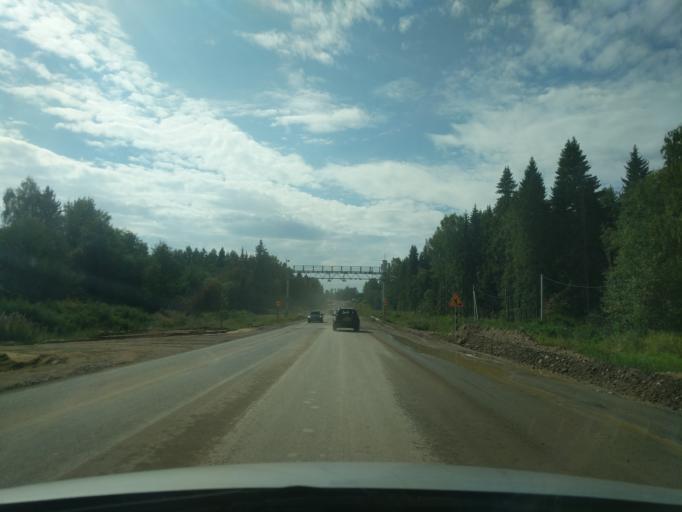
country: RU
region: Kostroma
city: Sudislavl'
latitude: 57.8779
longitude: 41.6834
